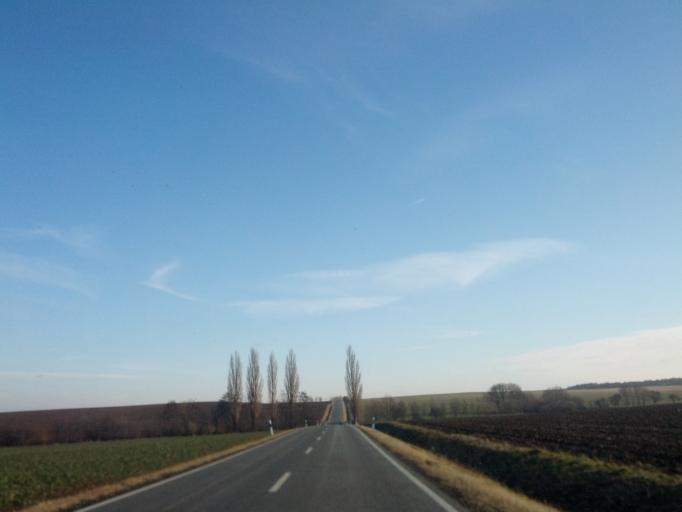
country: DE
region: Thuringia
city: Heroldishausen
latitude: 51.1084
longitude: 10.5352
